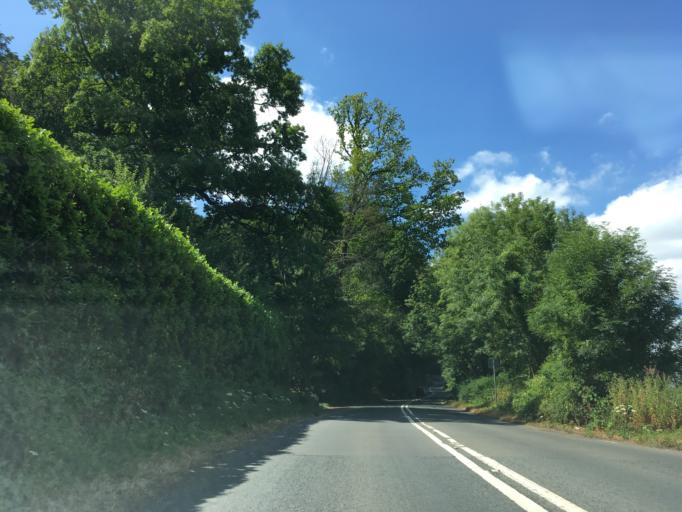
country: GB
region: England
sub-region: Gloucestershire
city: Churchdown
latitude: 51.8355
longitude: -2.1605
